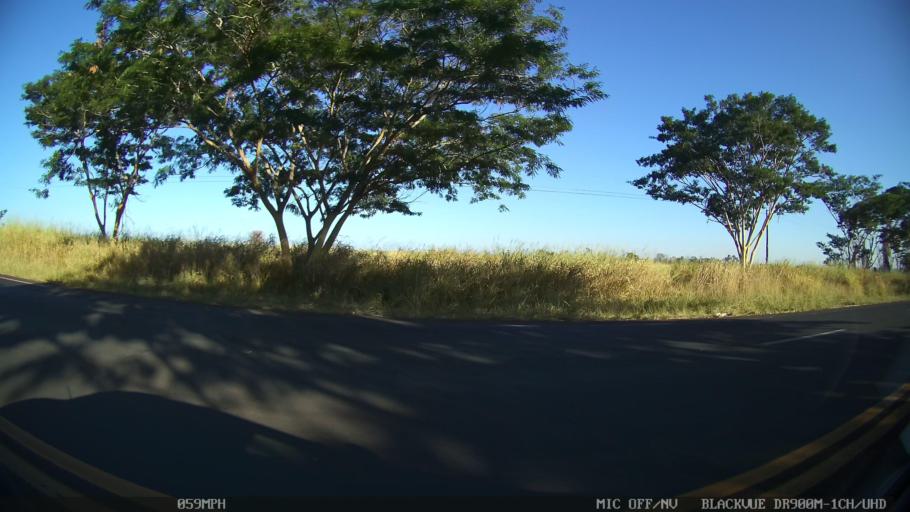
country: BR
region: Sao Paulo
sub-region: Olimpia
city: Olimpia
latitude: -20.7266
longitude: -49.0391
